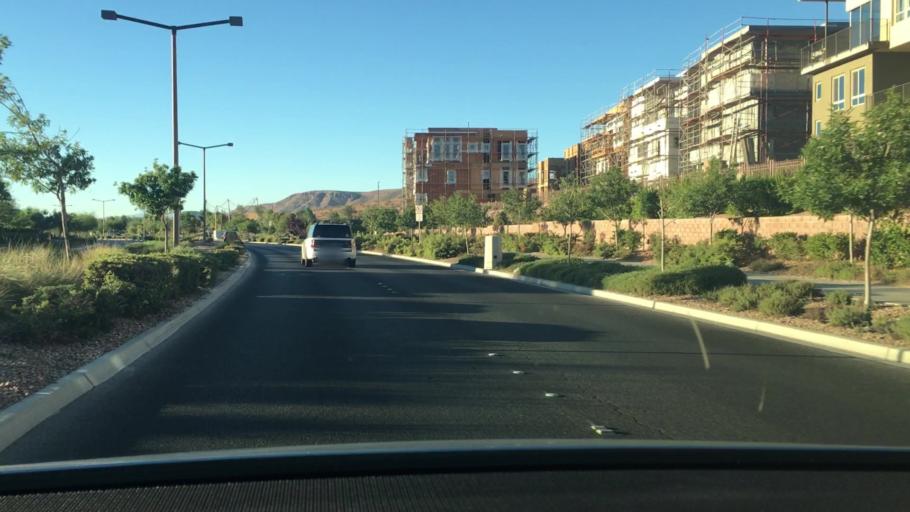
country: US
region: Nevada
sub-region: Clark County
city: Summerlin South
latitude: 36.1121
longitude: -115.3299
